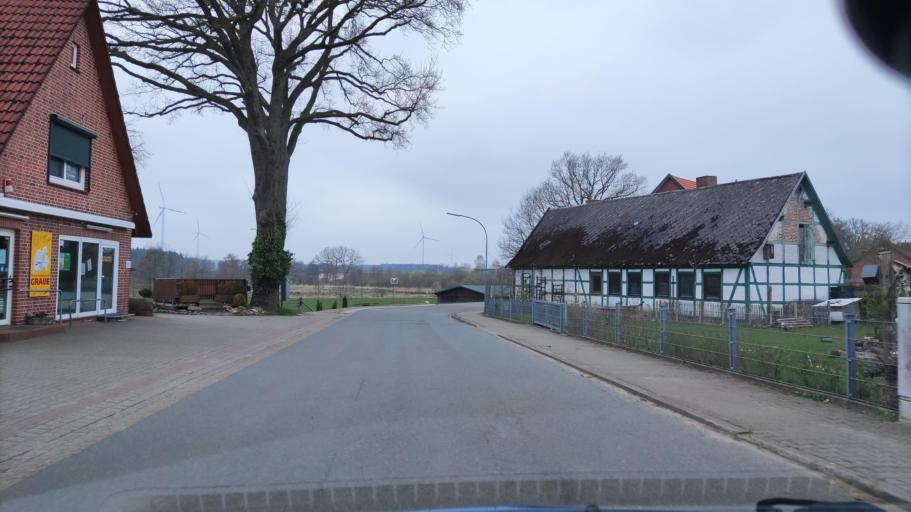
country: DE
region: Lower Saxony
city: Wulfsen
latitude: 53.2991
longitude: 10.1337
